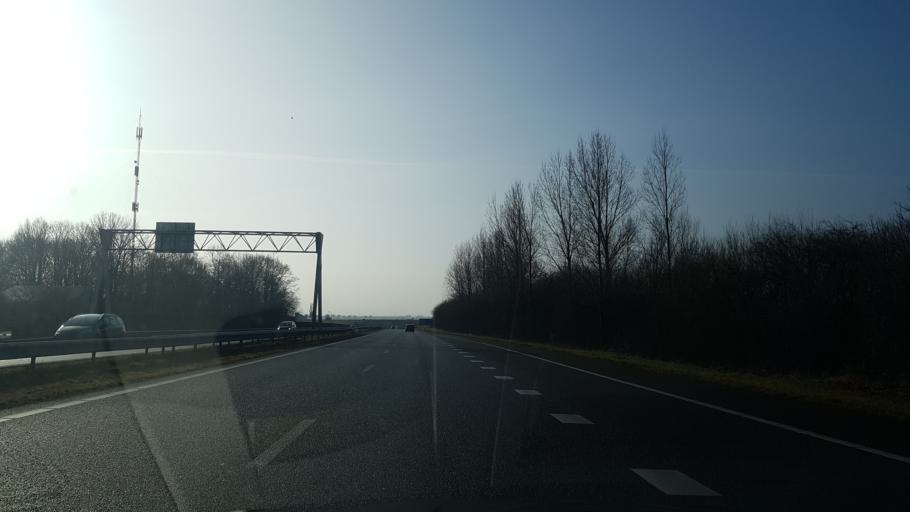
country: NL
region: Friesland
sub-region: Gemeente Boarnsterhim
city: Grou
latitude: 53.0847
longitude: 5.8258
